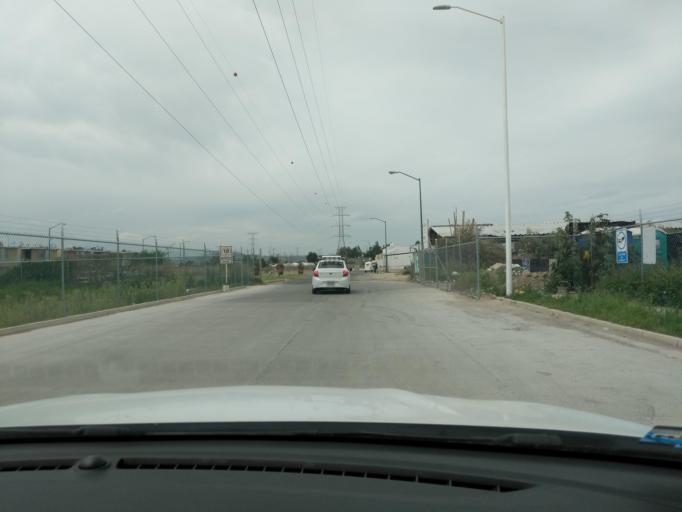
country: MX
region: Jalisco
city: Tesistan
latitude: 20.7858
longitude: -103.4884
